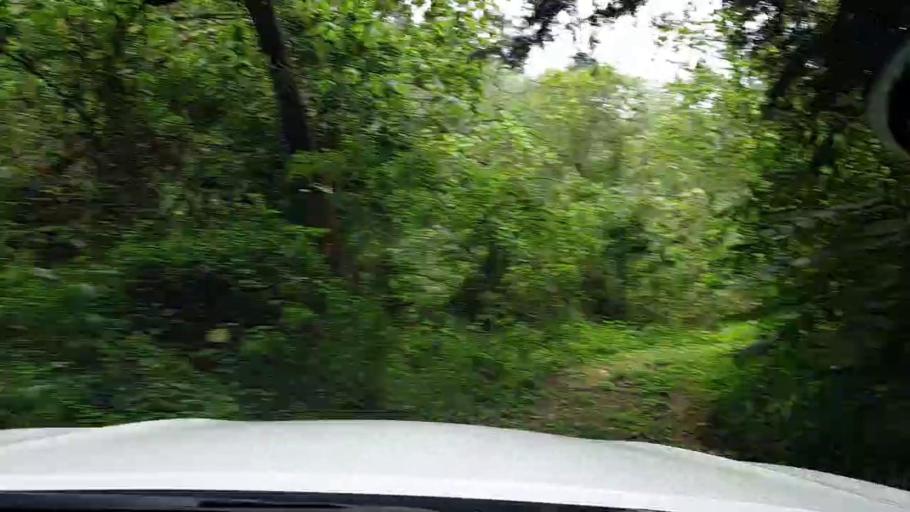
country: RW
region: Western Province
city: Kibuye
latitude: -2.2861
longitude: 29.3046
